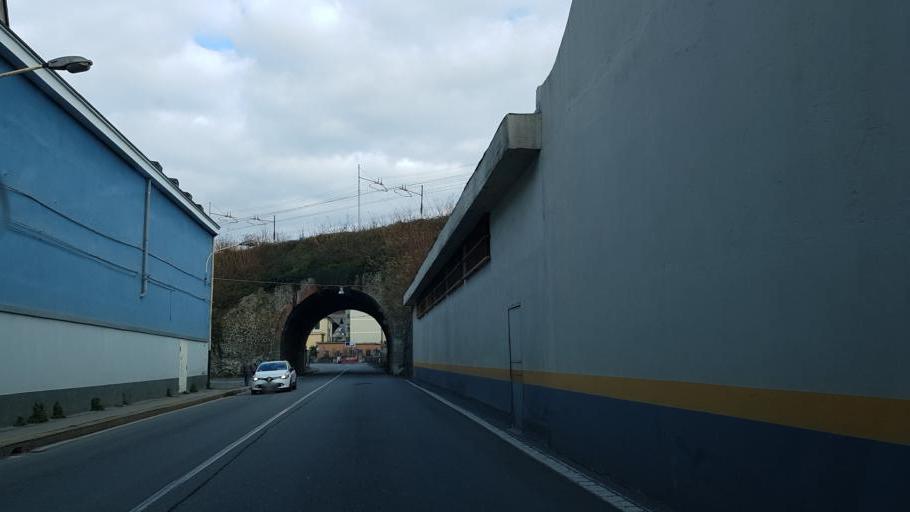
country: IT
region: Liguria
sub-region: Provincia di Genova
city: Genoa
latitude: 44.4392
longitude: 8.8880
